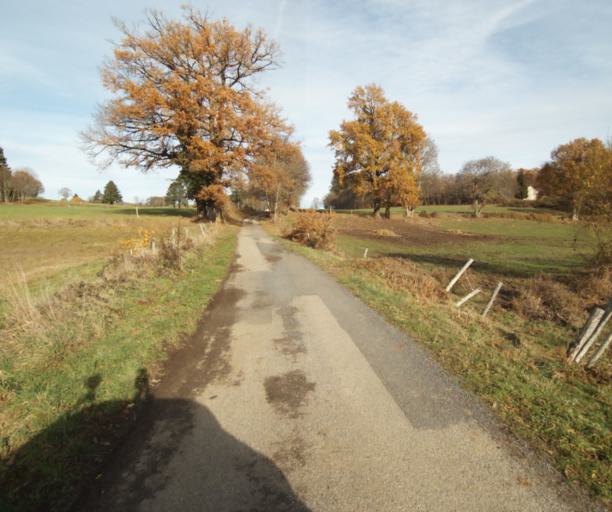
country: FR
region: Limousin
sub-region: Departement de la Correze
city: Sainte-Fortunade
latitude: 45.1970
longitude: 1.7467
